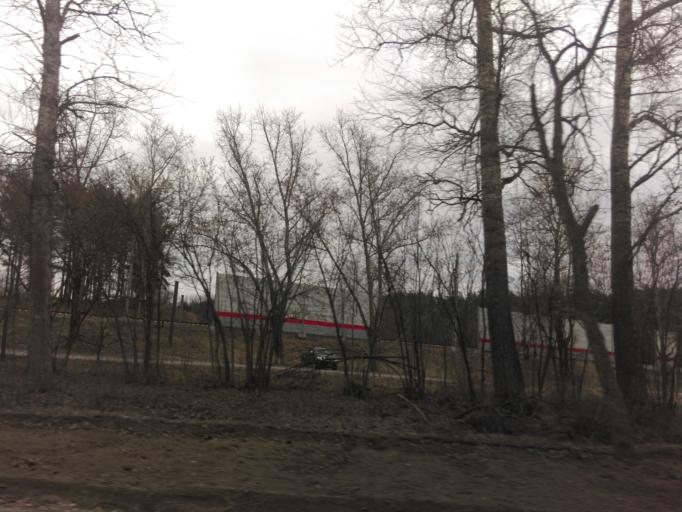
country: RU
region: Moskovskaya
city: Barvikha
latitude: 55.7477
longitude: 37.3090
